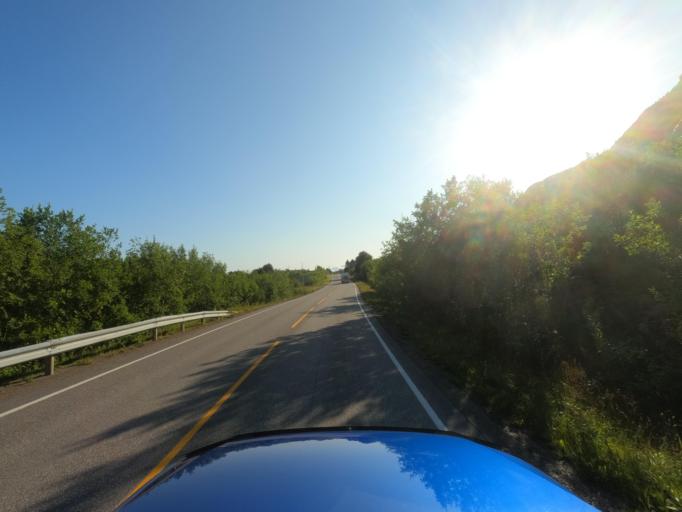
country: NO
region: Nordland
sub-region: Moskenes
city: Reine
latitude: 67.9111
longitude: 13.0408
